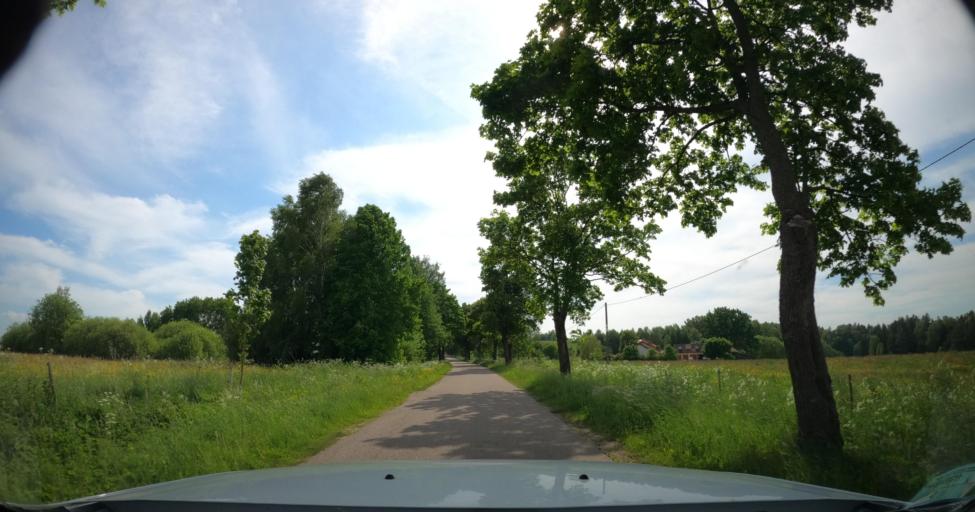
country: PL
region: Warmian-Masurian Voivodeship
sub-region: Powiat lidzbarski
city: Lubomino
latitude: 54.0949
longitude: 20.3093
